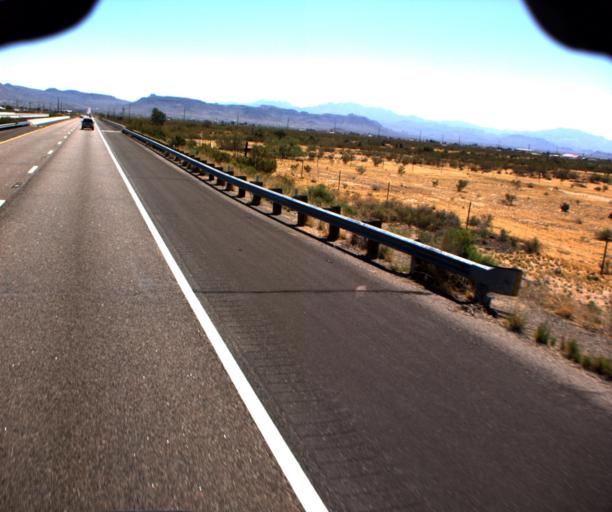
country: US
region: Arizona
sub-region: Mohave County
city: Golden Valley
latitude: 35.2234
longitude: -114.2466
